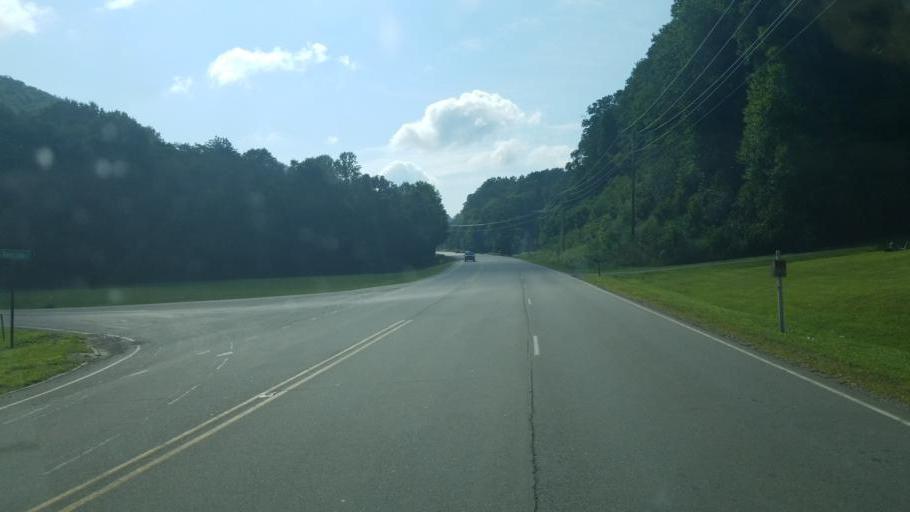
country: US
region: North Carolina
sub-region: Avery County
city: Newland
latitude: 36.1507
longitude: -81.9611
